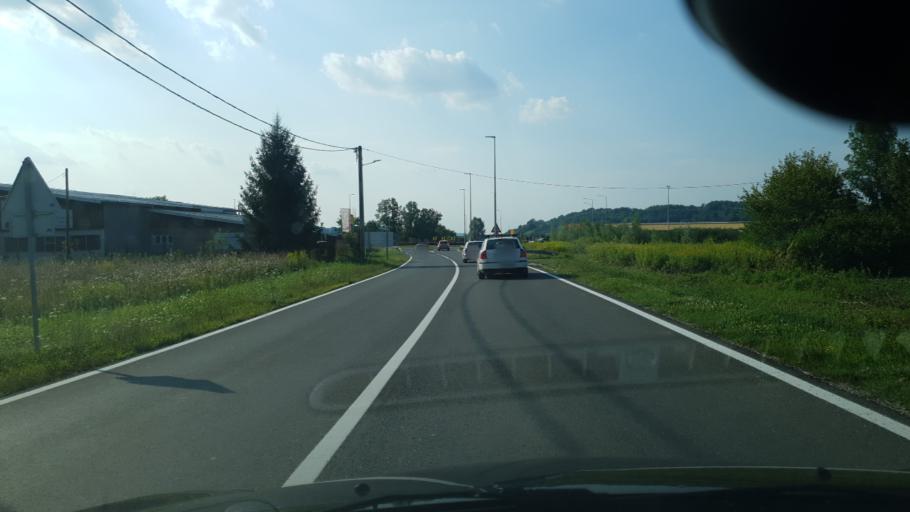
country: HR
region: Krapinsko-Zagorska
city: Oroslavje
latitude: 46.0037
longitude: 15.8815
